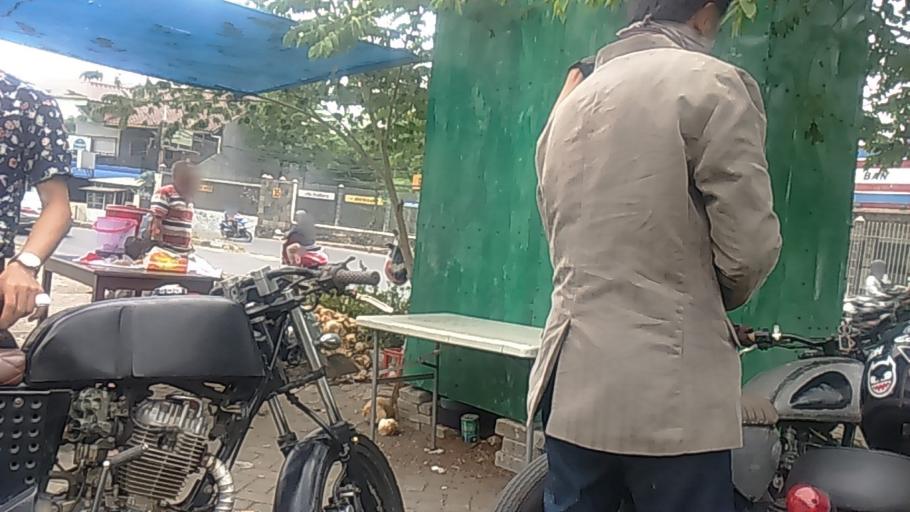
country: ID
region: West Java
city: Pamulang
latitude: -6.3052
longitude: 106.7744
